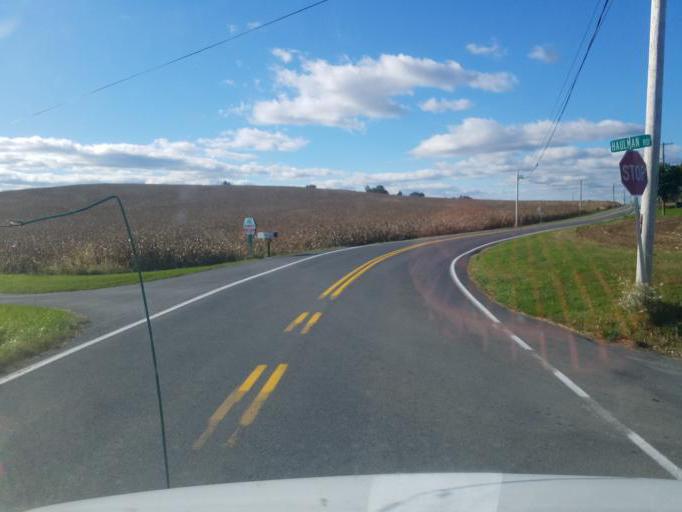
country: US
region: Pennsylvania
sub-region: Franklin County
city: Mont Alto
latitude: 39.8694
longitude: -77.5789
